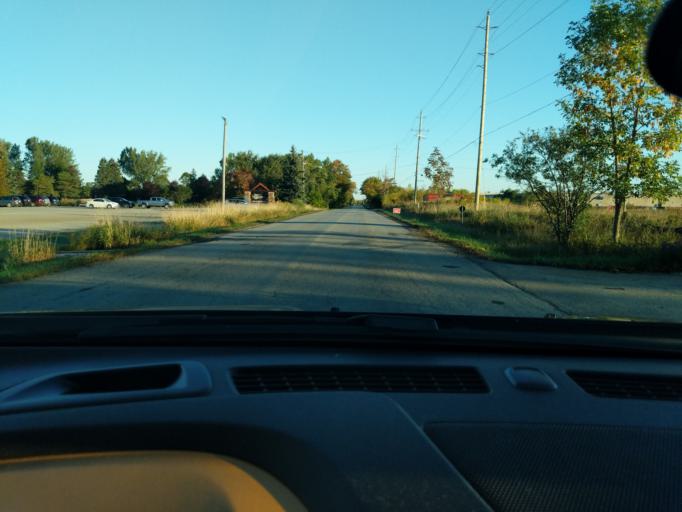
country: CA
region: Ontario
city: Collingwood
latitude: 44.4946
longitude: -80.2495
